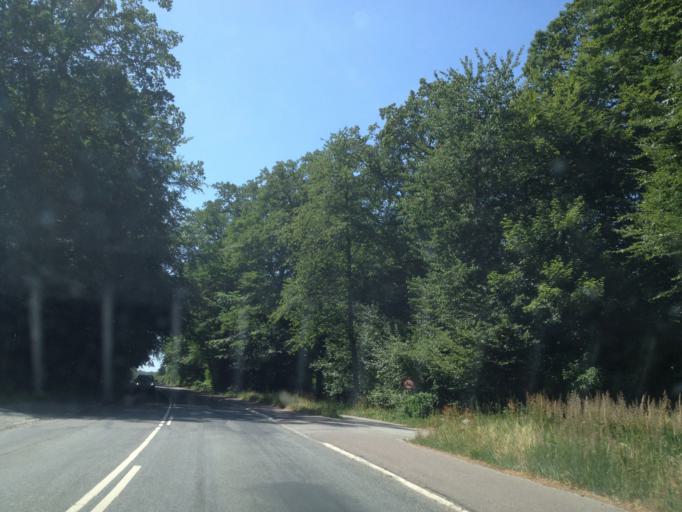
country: DK
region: Capital Region
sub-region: Rudersdal Kommune
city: Trorod
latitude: 55.8195
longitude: 12.5485
